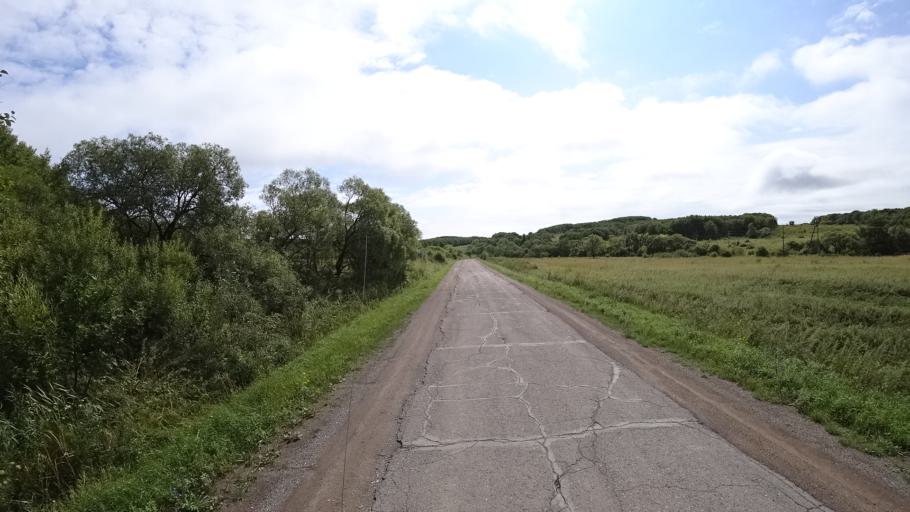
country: RU
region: Primorskiy
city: Lyalichi
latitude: 44.1516
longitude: 132.3912
